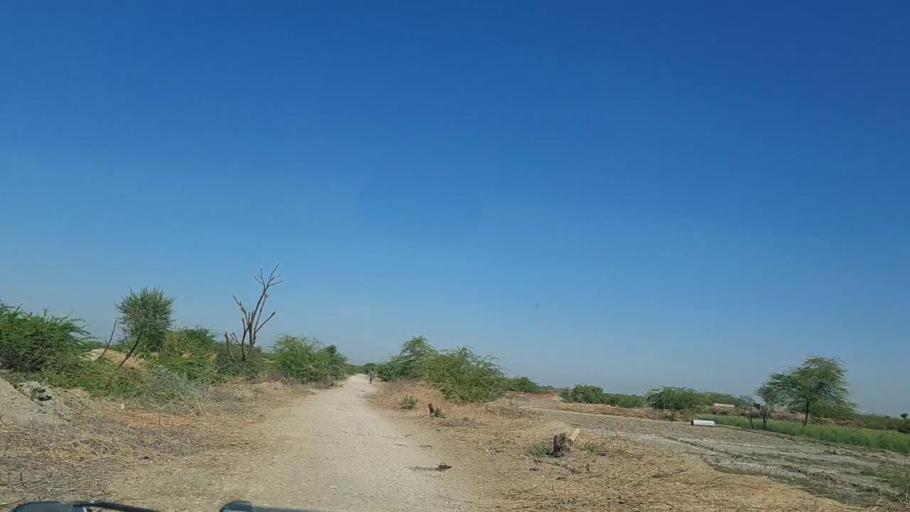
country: PK
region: Sindh
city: Dhoro Naro
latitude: 25.4628
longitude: 69.5135
